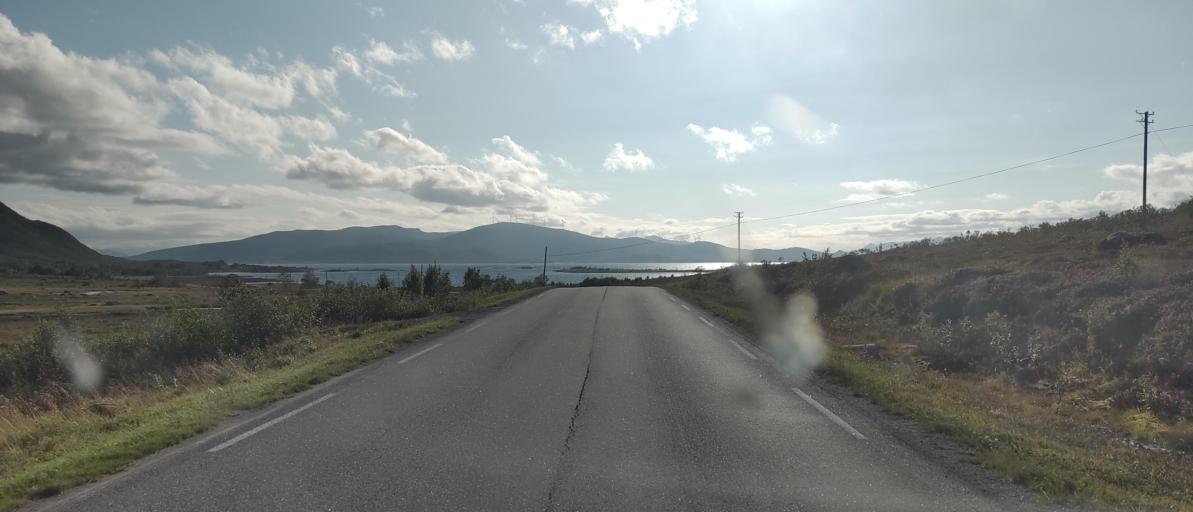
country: NO
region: Nordland
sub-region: Sortland
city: Sortland
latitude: 68.7883
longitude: 15.4951
